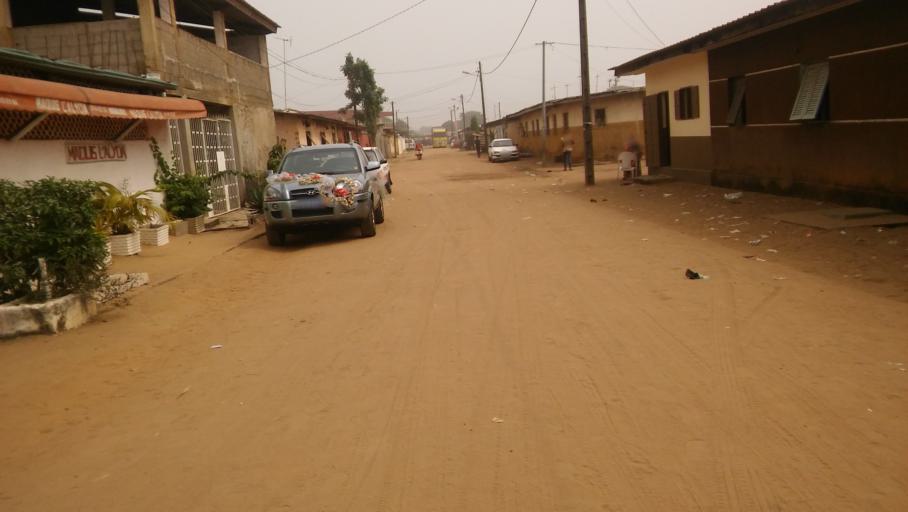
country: CI
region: Sud-Comoe
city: Grand-Bassam
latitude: 5.2136
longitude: -3.7342
